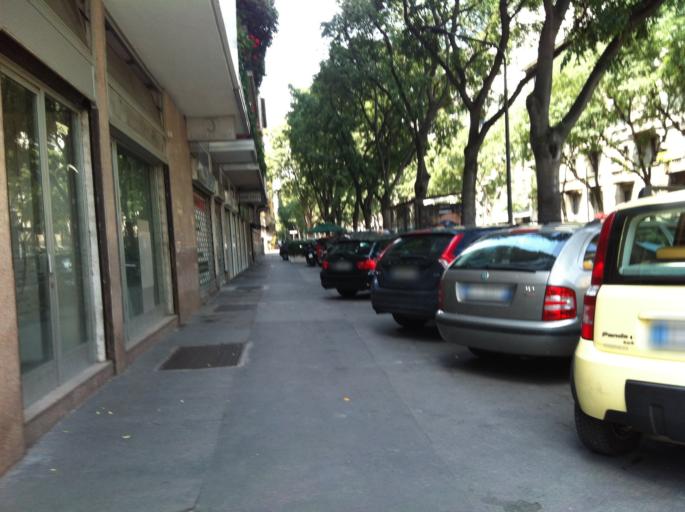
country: IT
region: Lombardy
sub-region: Citta metropolitana di Milano
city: Milano
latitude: 45.4759
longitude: 9.2147
